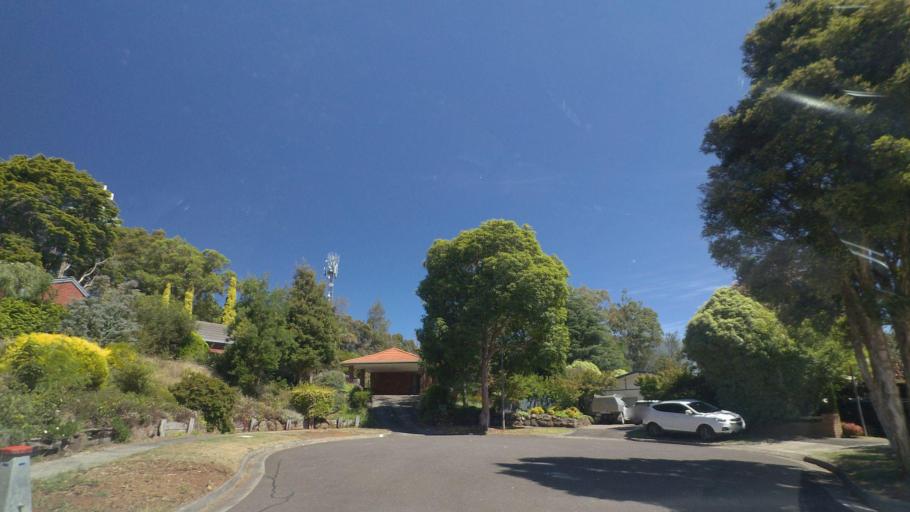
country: AU
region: Victoria
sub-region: Yarra Ranges
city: Chirnside Park
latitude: -37.7609
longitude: 145.3254
